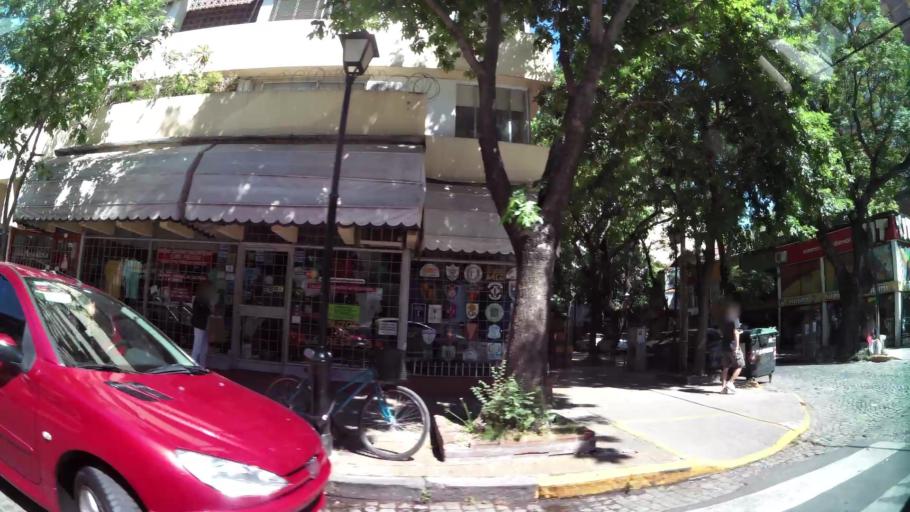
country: AR
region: Buenos Aires
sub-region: Partido de San Isidro
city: San Isidro
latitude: -34.4713
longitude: -58.5117
